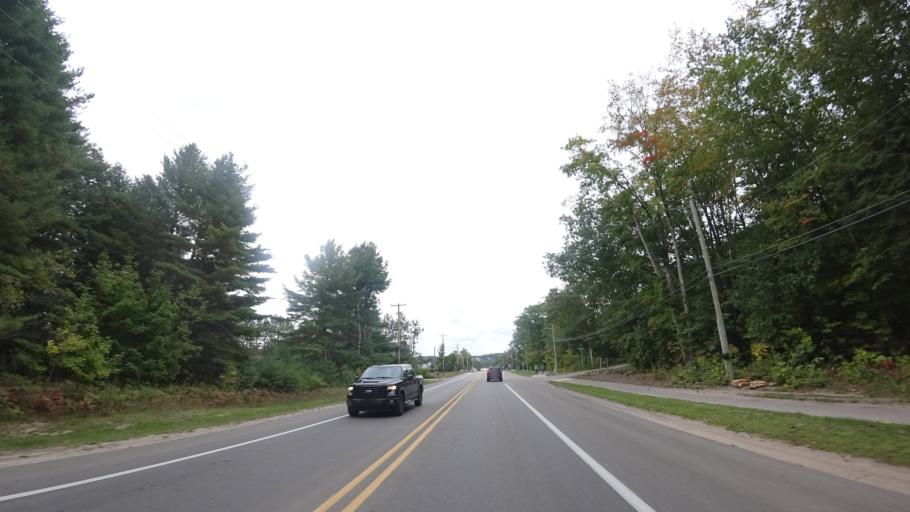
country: US
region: Michigan
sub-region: Emmet County
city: Petoskey
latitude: 45.4068
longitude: -84.9021
